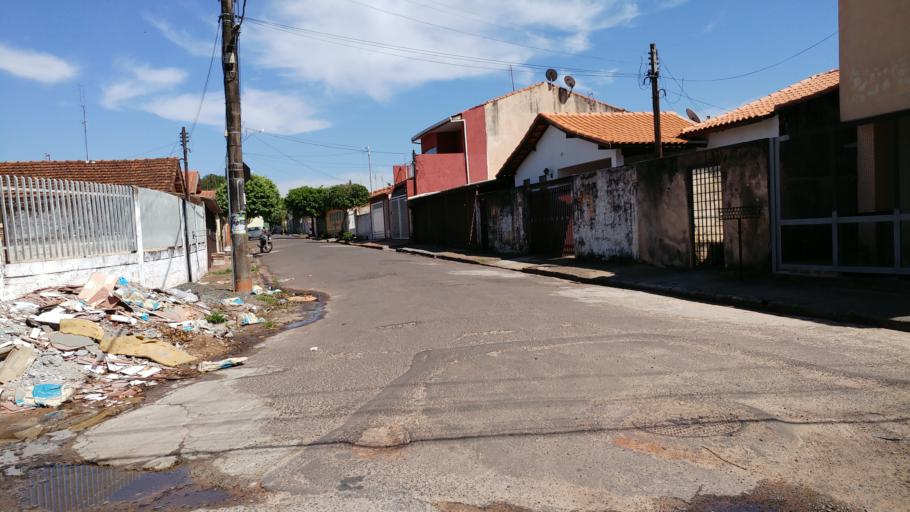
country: BR
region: Sao Paulo
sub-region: Paraguacu Paulista
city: Paraguacu Paulista
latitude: -22.4282
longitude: -50.5783
